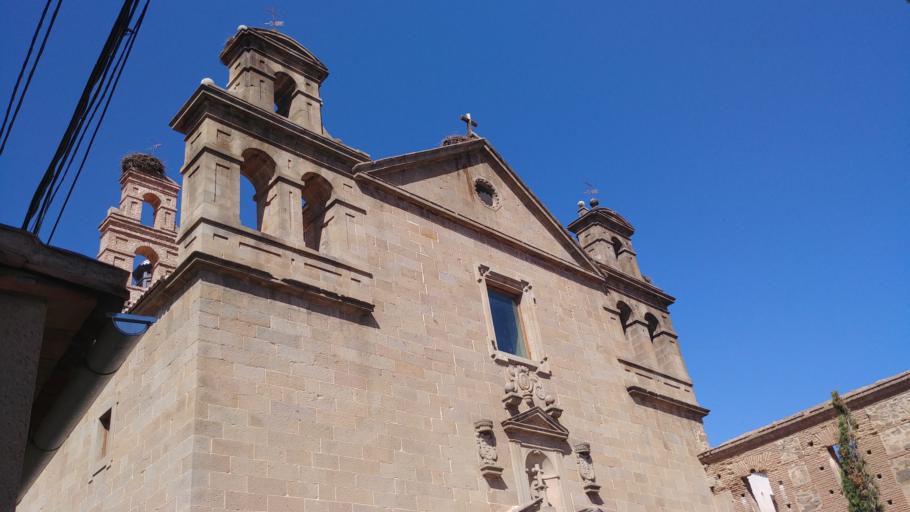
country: ES
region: Castille-La Mancha
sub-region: Province of Toledo
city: Oropesa
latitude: 39.9189
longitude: -5.1721
